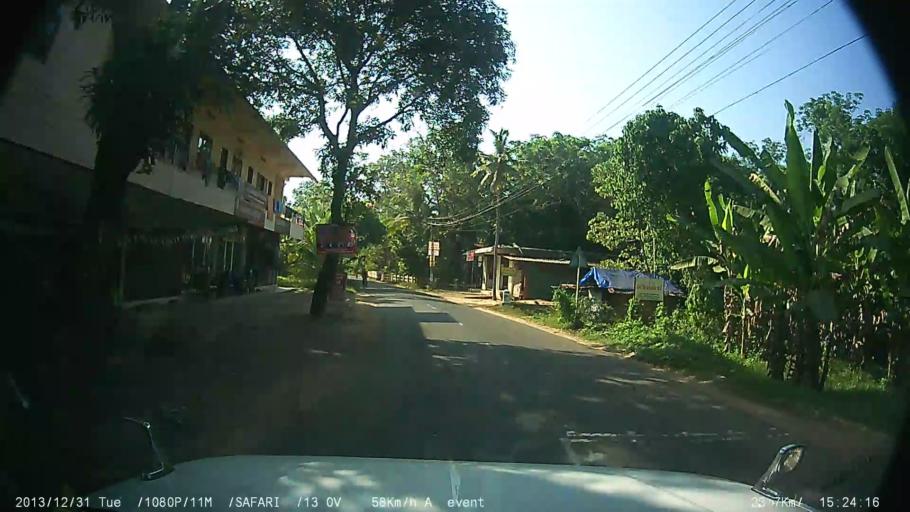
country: IN
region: Kerala
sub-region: Kottayam
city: Vaikam
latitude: 9.6930
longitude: 76.4690
